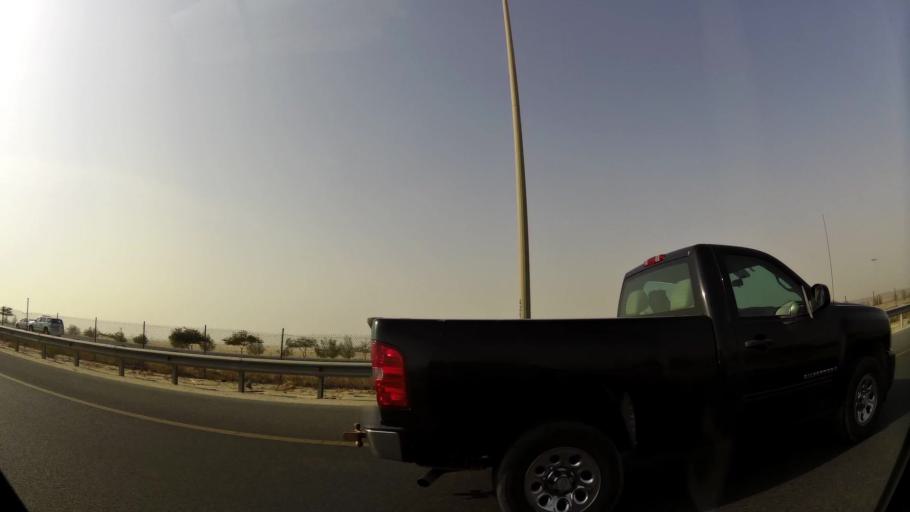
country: KW
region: Mubarak al Kabir
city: Mubarak al Kabir
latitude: 29.1776
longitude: 48.0331
